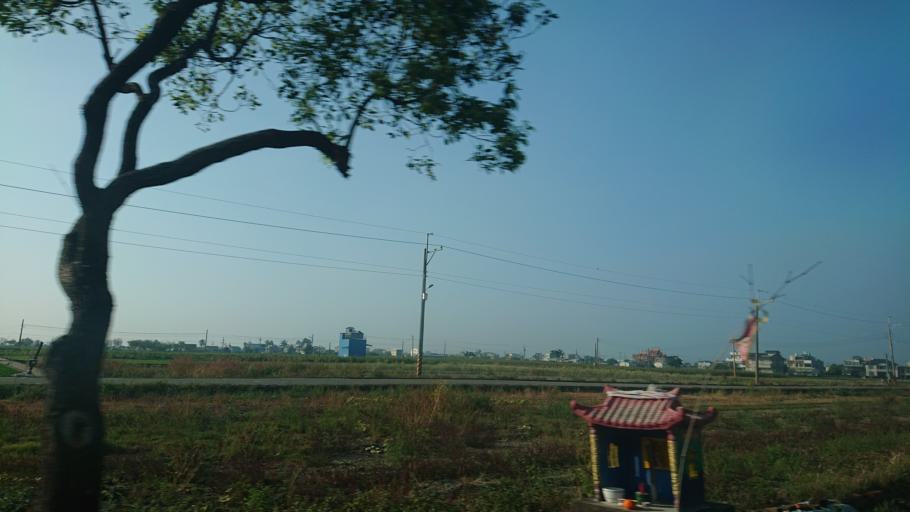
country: TW
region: Taiwan
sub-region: Tainan
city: Tainan
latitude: 23.1296
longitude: 120.2311
